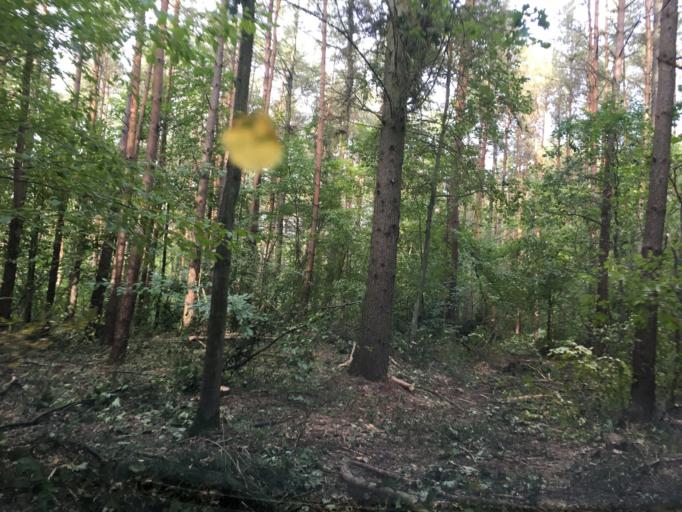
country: PL
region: Kujawsko-Pomorskie
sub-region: Powiat brodnicki
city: Gorzno
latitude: 53.2245
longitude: 19.7172
